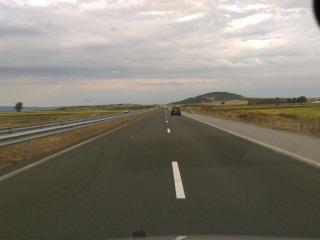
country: BG
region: Yambol
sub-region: Obshtina Yambol
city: Yambol
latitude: 42.5423
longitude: 26.4360
